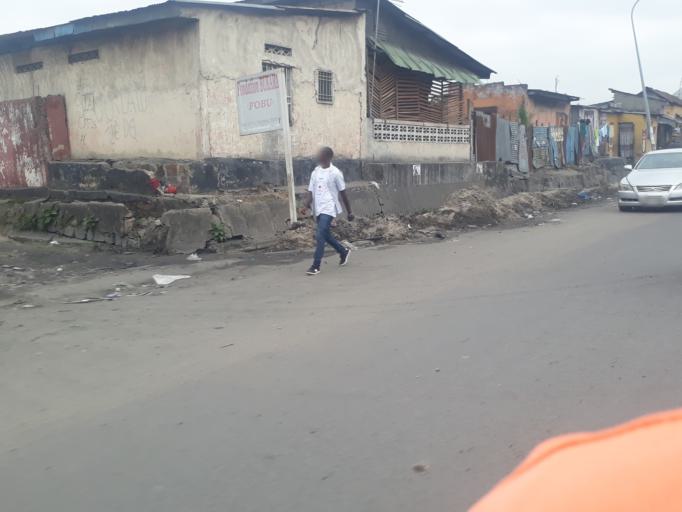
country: CD
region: Kinshasa
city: Kinshasa
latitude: -4.3179
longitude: 15.3107
